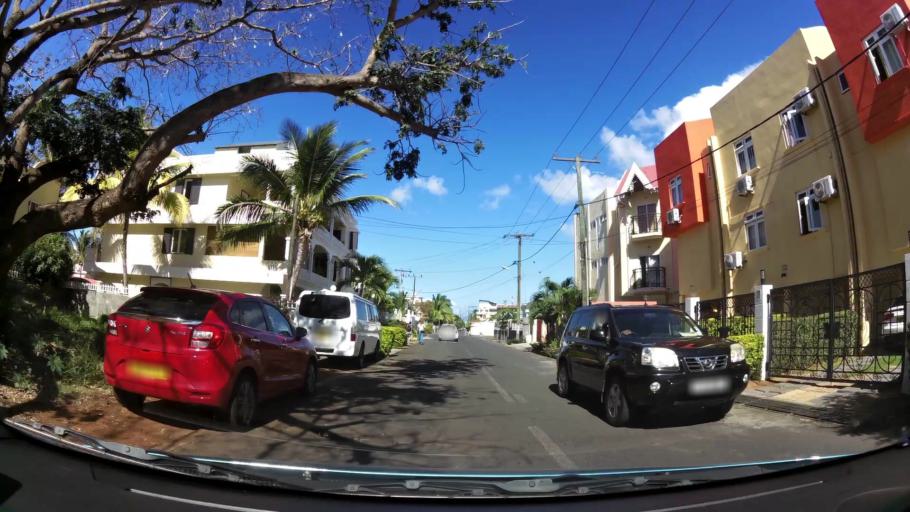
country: MU
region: Black River
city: Flic en Flac
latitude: -20.2847
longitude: 57.3677
